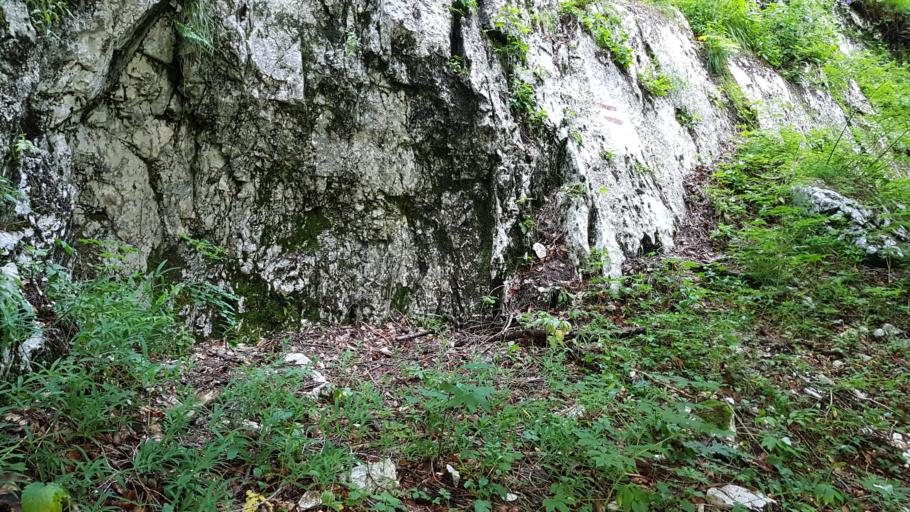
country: SI
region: Bovec
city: Bovec
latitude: 46.3888
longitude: 13.4973
